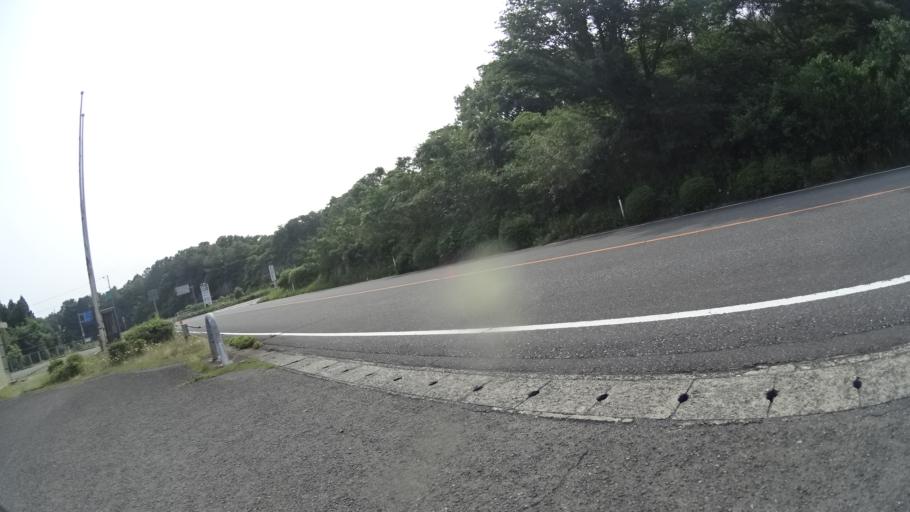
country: JP
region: Yamaguchi
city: Ogori-shimogo
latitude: 34.2352
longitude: 131.3096
